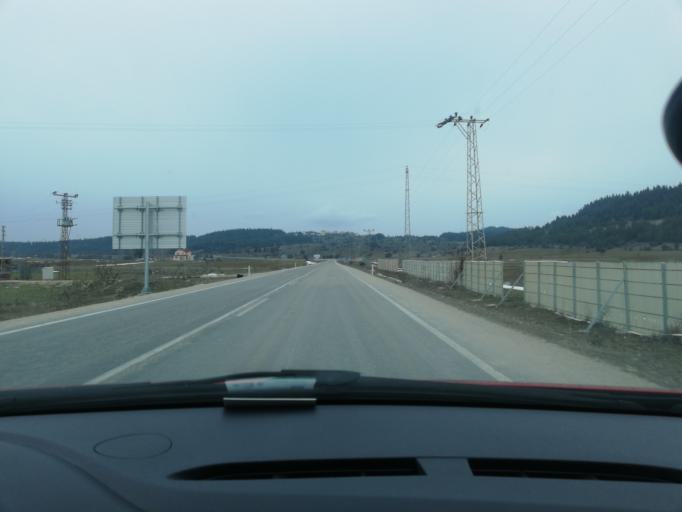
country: TR
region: Kastamonu
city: Agli
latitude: 41.6917
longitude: 33.5535
